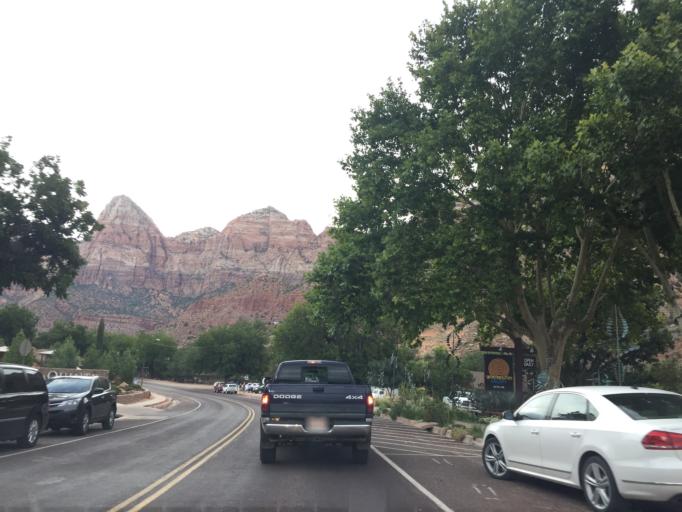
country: US
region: Utah
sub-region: Washington County
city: Hildale
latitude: 37.1892
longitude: -112.9969
